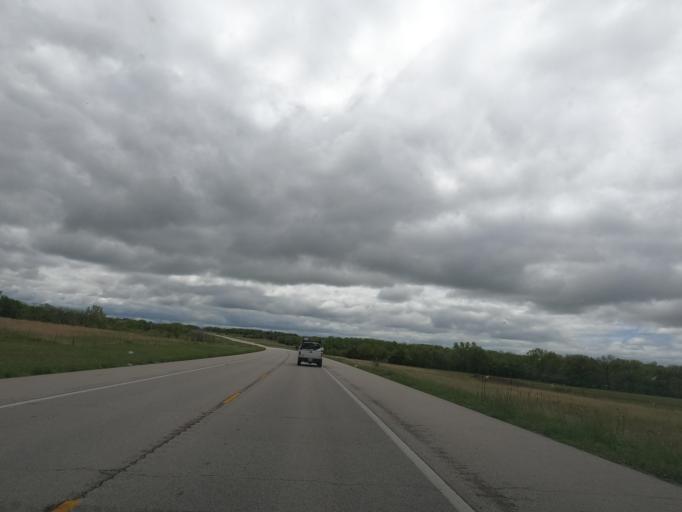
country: US
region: Kansas
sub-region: Wilson County
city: Fredonia
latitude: 37.5198
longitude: -95.8007
